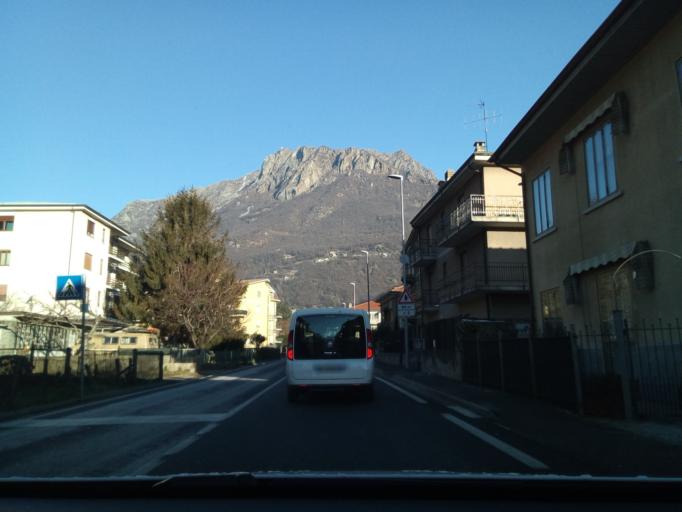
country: IT
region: Aosta Valley
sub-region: Valle d'Aosta
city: Pont-Saint-Martin
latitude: 45.5890
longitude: 7.8010
